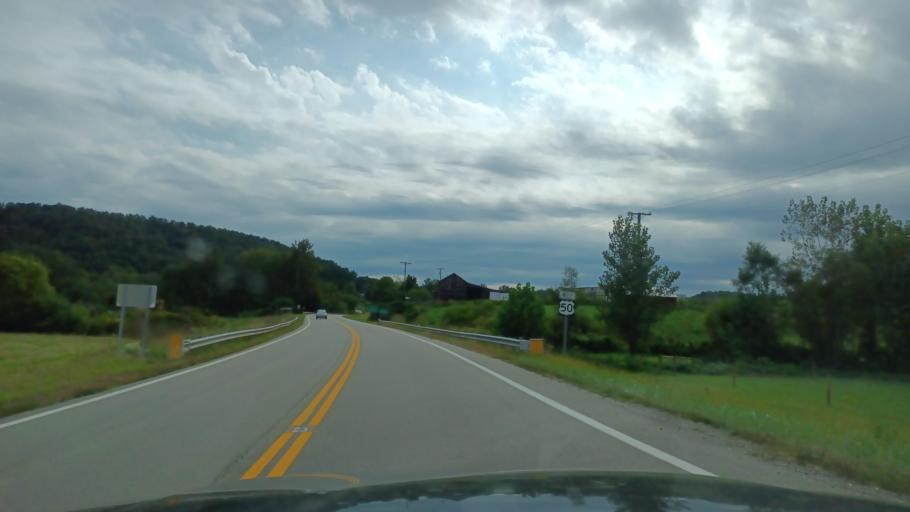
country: US
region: Ohio
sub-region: Vinton County
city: McArthur
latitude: 39.2676
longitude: -82.6794
